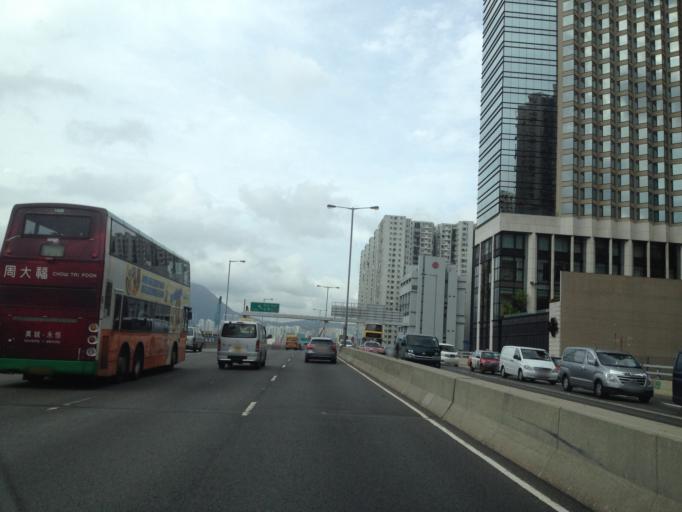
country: HK
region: Wanchai
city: Wan Chai
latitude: 22.2884
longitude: 114.1905
